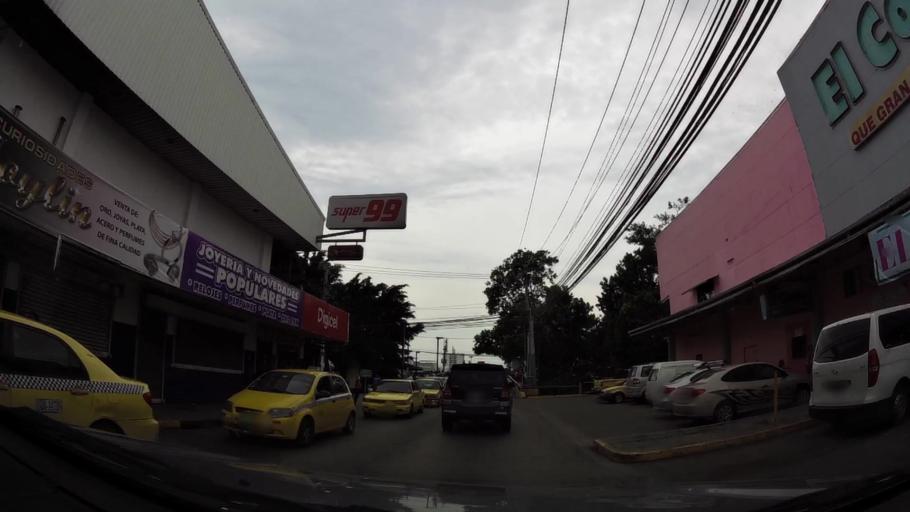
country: PA
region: Panama
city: San Miguelito
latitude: 9.0483
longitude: -79.4512
